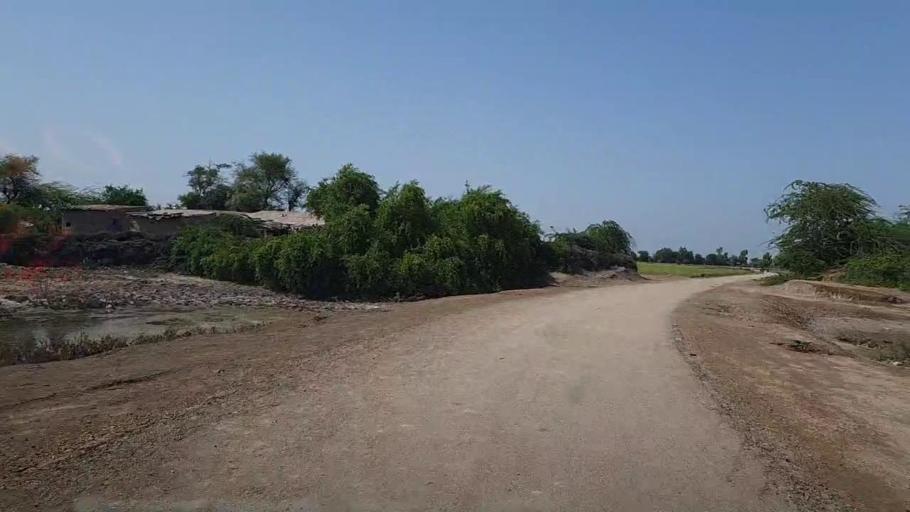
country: PK
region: Sindh
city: Kario
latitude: 24.8761
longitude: 68.6828
